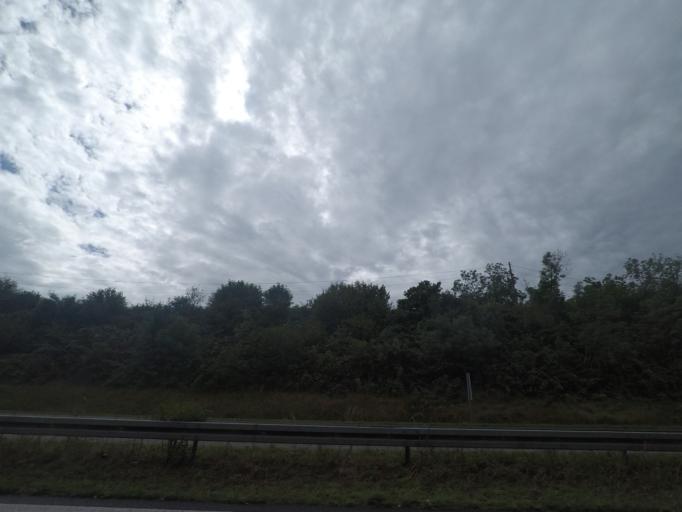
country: DE
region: Baden-Wuerttemberg
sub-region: Freiburg Region
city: Eimeldingen
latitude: 47.6244
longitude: 7.5974
